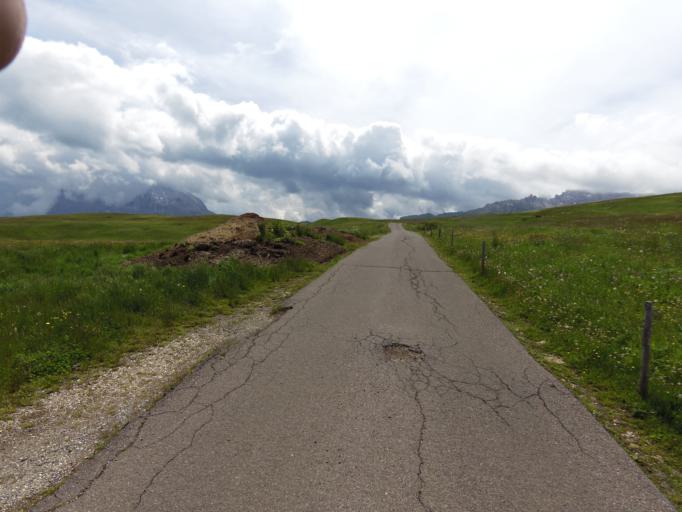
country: IT
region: Trentino-Alto Adige
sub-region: Bolzano
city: Ortisei
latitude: 46.5342
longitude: 11.6271
